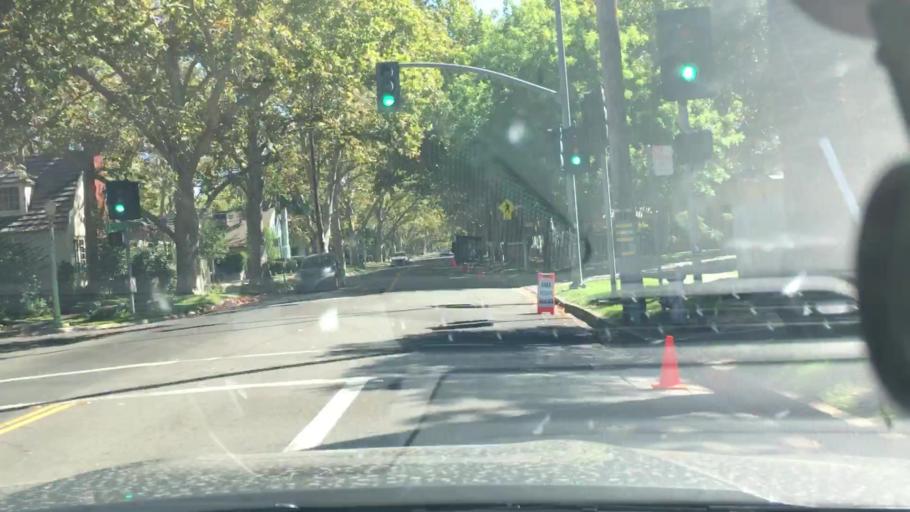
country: US
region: California
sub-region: Sacramento County
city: Sacramento
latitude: 38.5741
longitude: -121.4608
